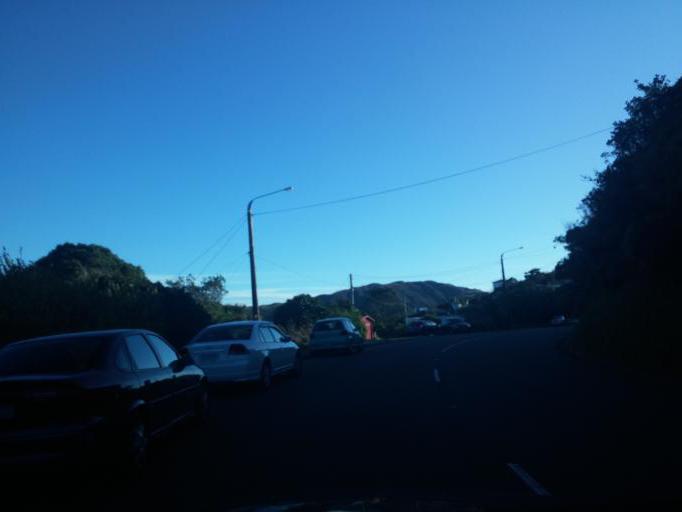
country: NZ
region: Wellington
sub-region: Wellington City
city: Kelburn
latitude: -41.2761
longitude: 174.7593
